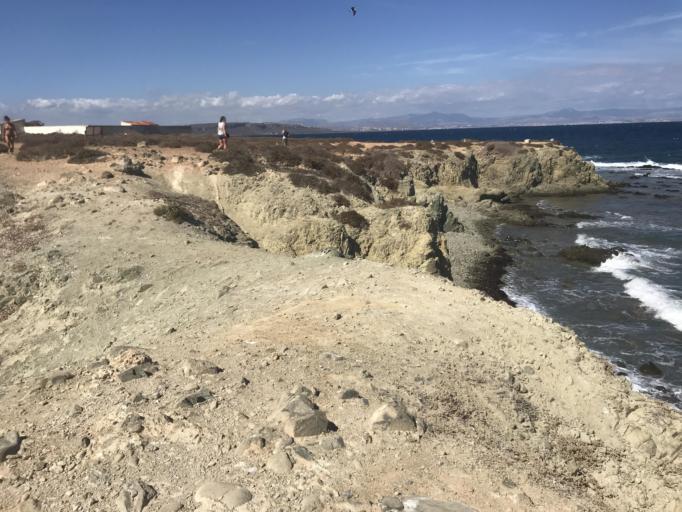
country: ES
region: Valencia
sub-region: Provincia de Alicante
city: Santa Pola
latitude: 38.1630
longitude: -0.4649
